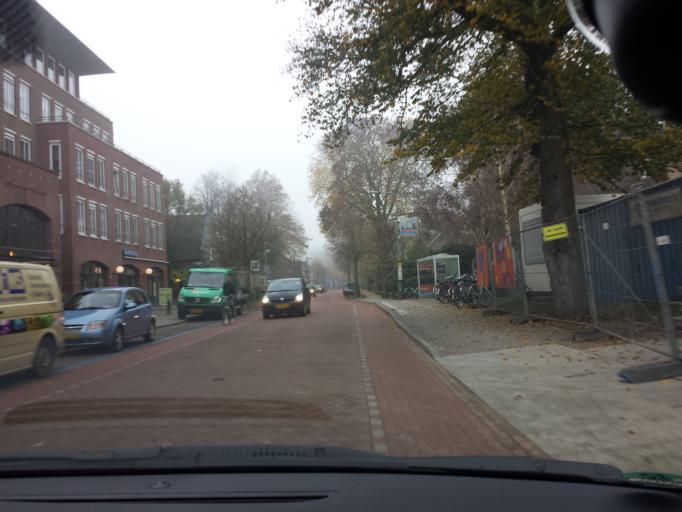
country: NL
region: Limburg
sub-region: Gemeente Peel en Maas
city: Maasbree
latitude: 51.3293
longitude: 5.9783
